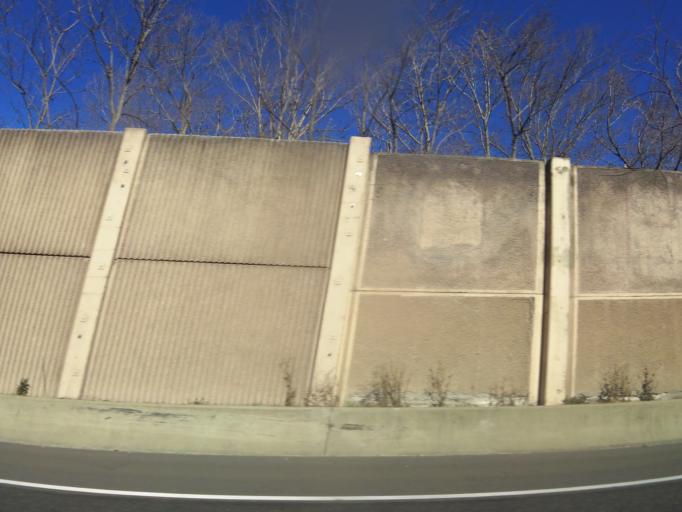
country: US
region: Virginia
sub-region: City of Portsmouth
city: Portsmouth Heights
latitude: 36.8687
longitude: -76.4128
